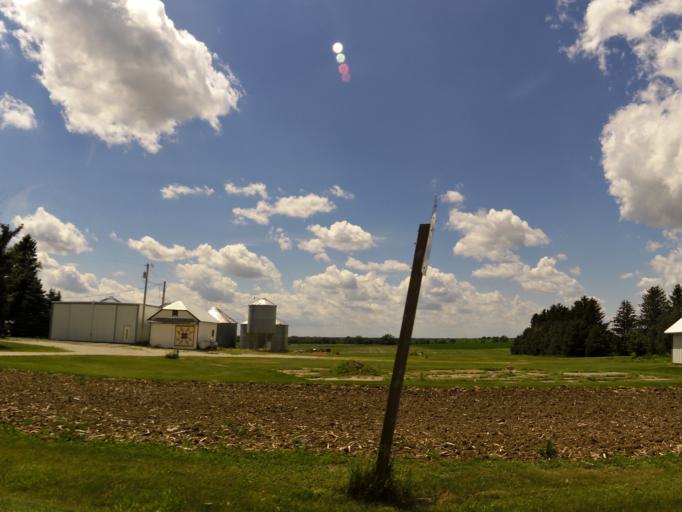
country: US
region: Iowa
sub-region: Buchanan County
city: Independence
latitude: 42.5101
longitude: -91.8898
